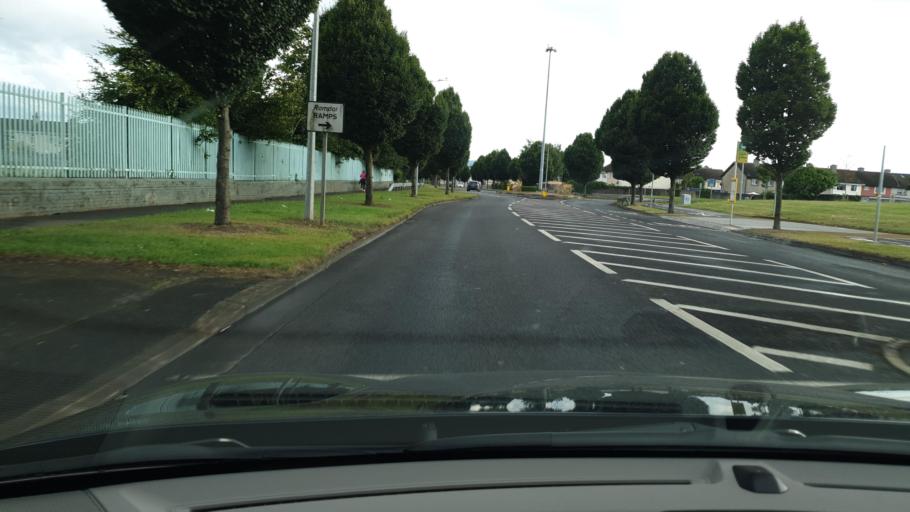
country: IE
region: Leinster
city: Clondalkin
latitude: 53.3414
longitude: -6.3990
